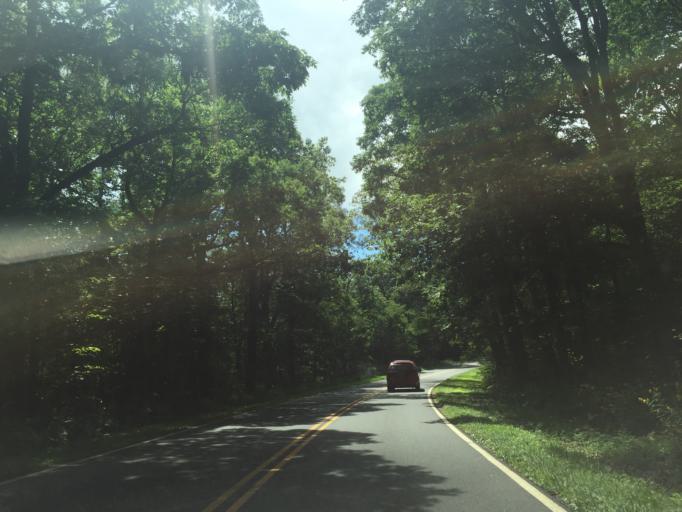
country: US
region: Virginia
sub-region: Rappahannock County
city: Washington
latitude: 38.7629
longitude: -78.2396
